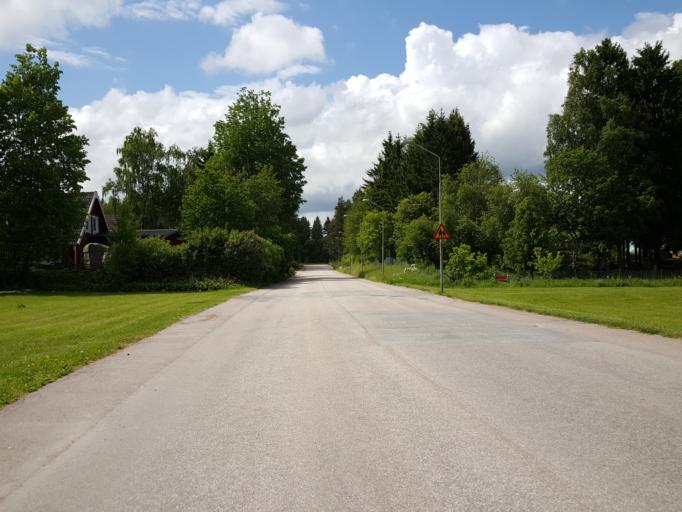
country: SE
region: Uppsala
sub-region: Osthammars Kommun
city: Gimo
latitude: 60.1684
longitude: 18.1758
